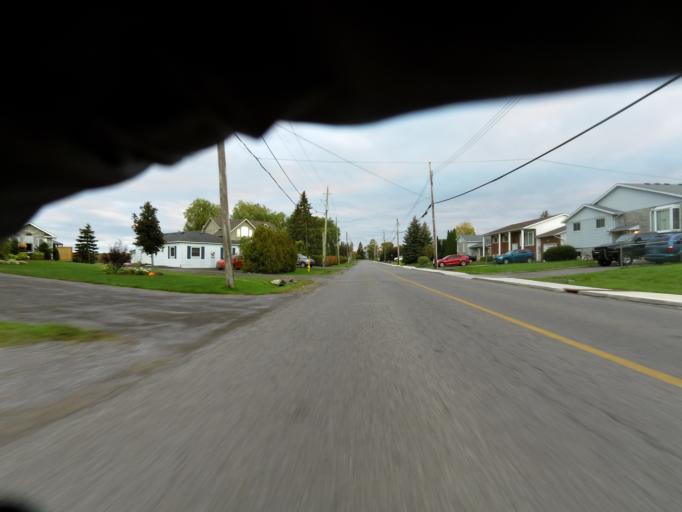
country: CA
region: Ontario
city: Quinte West
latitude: 44.0230
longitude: -77.7287
